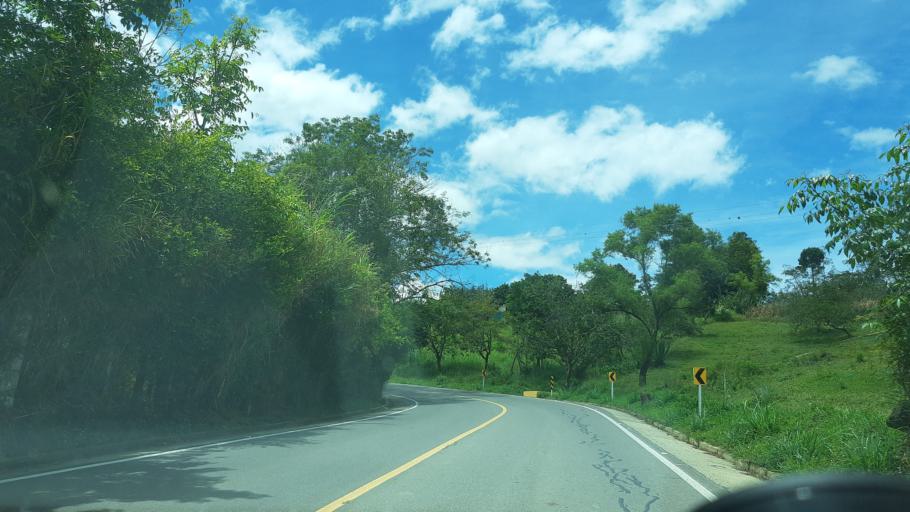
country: CO
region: Boyaca
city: Guateque
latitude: 5.0084
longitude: -73.4521
